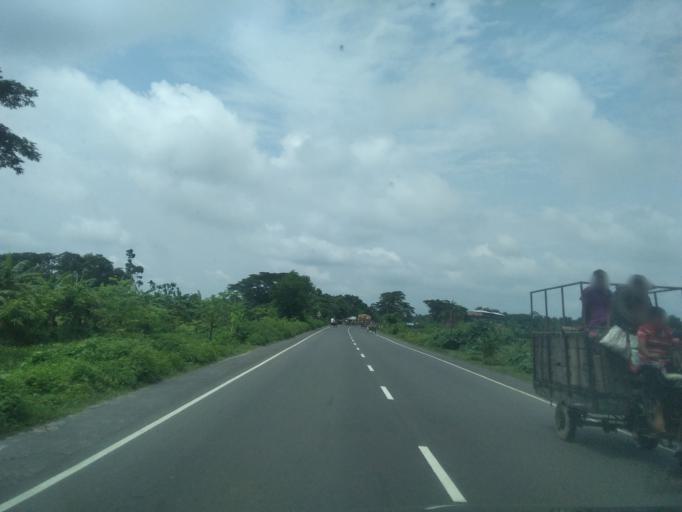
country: BD
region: Khulna
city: Kesabpur
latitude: 22.8083
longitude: 89.2410
